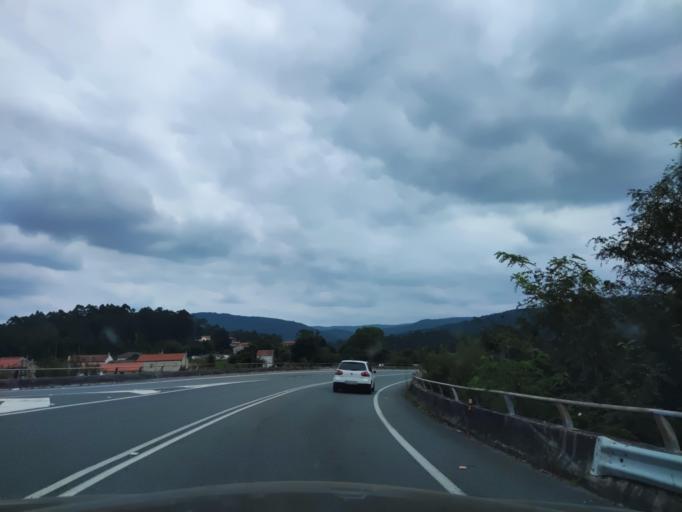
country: ES
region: Galicia
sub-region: Provincia da Coruna
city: Padron
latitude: 42.7322
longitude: -8.6574
